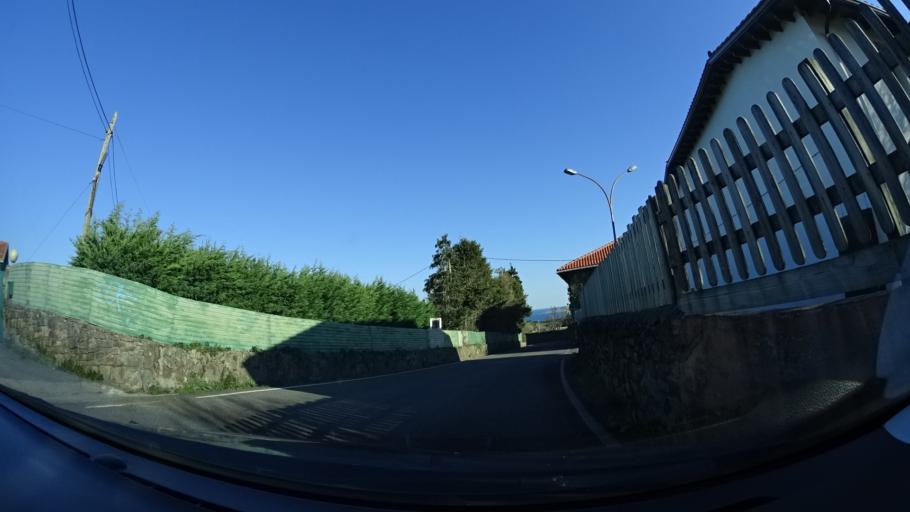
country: ES
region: Basque Country
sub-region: Bizkaia
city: Bermeo
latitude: 43.4248
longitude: -2.7354
